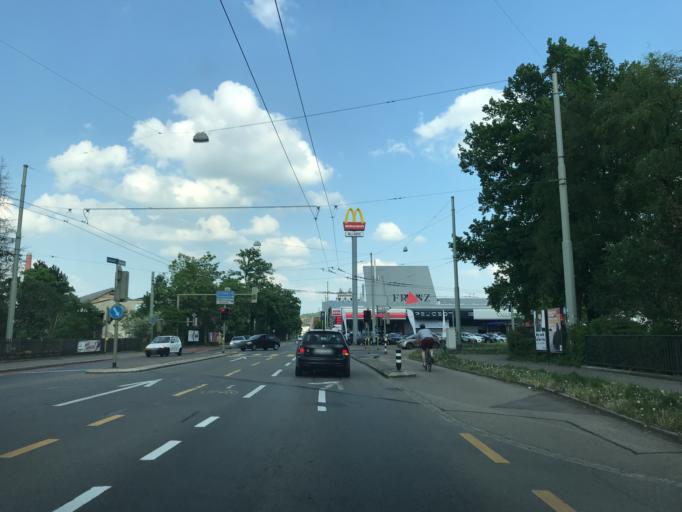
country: CH
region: Zurich
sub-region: Bezirk Winterthur
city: Mattenbach (Kreis 7) / Deutweg
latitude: 47.4982
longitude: 8.7450
